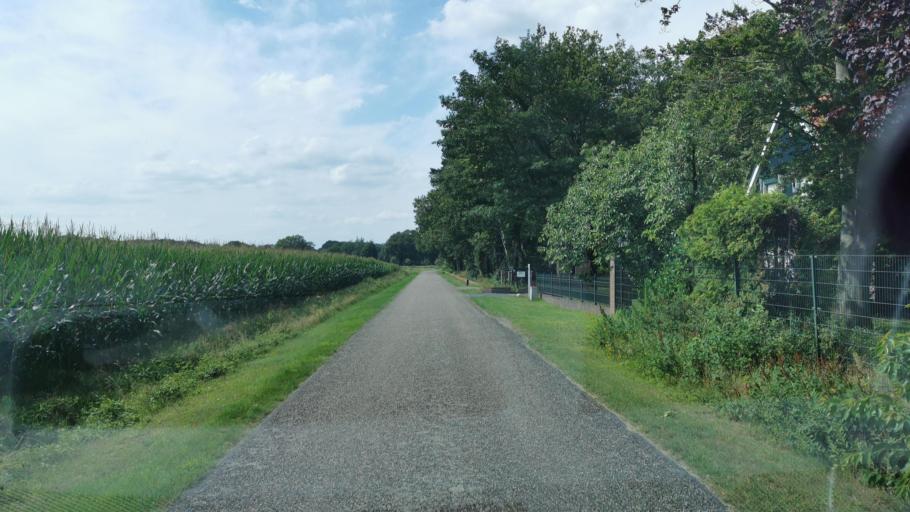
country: NL
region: Overijssel
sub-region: Gemeente Enschede
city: Enschede
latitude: 52.1683
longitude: 6.8853
